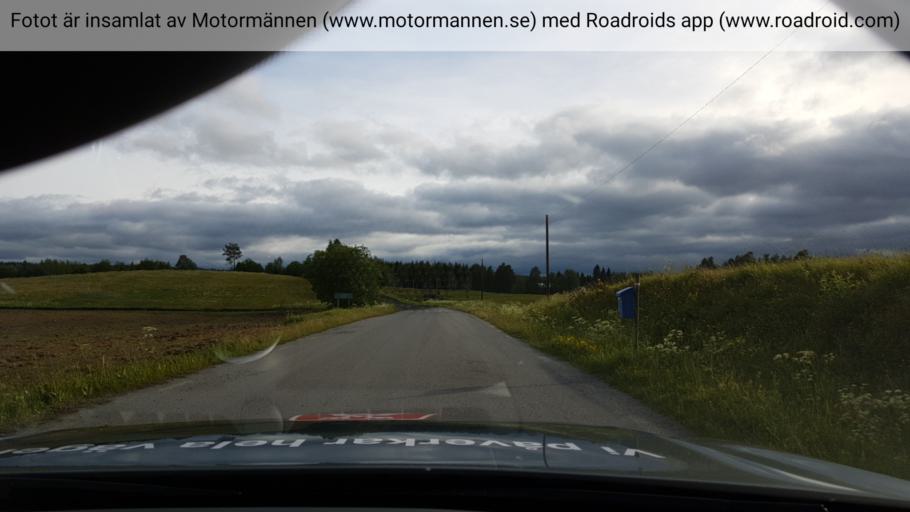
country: SE
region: Jaemtland
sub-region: OEstersunds Kommun
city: Lit
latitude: 63.6631
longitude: 15.0912
